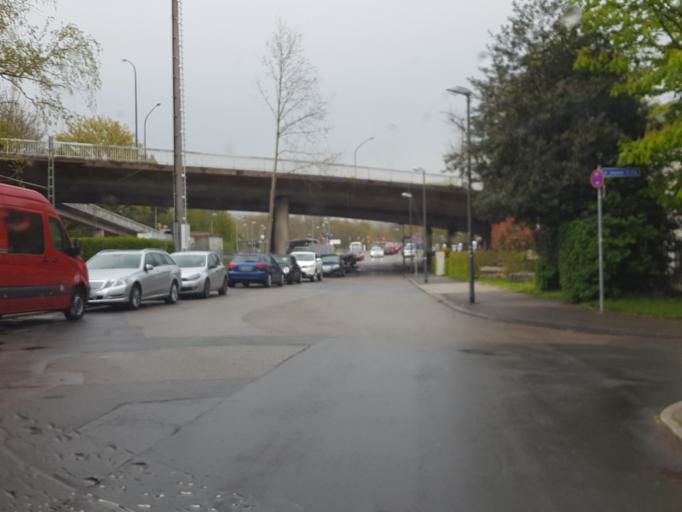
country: DE
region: North Rhine-Westphalia
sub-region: Regierungsbezirk Dusseldorf
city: Heiligenhaus
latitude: 51.3846
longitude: 6.9971
